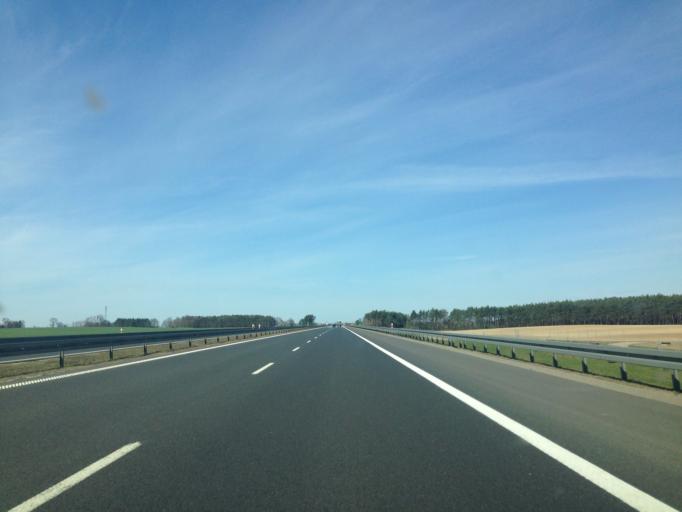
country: PL
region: Pomeranian Voivodeship
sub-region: Powiat starogardzki
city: Smetowo Graniczne
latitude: 53.7787
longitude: 18.6308
